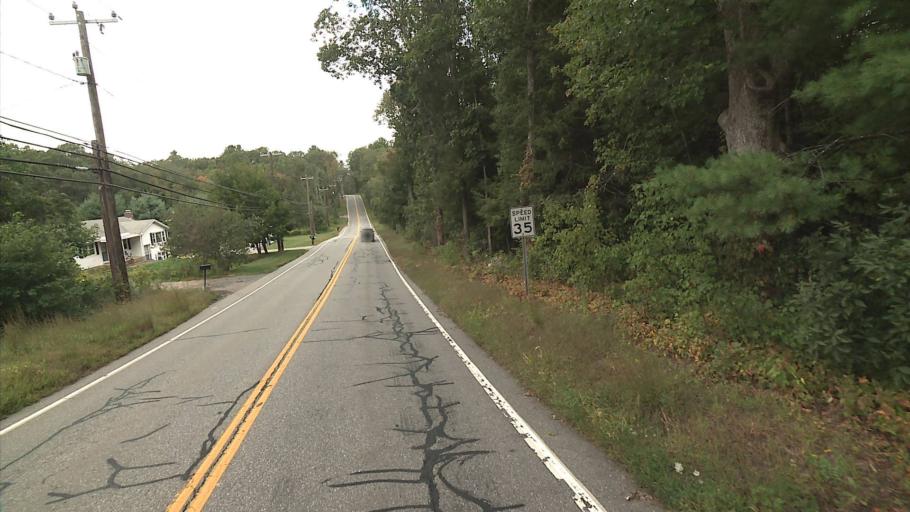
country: US
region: Connecticut
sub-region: Tolland County
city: Storrs
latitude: 41.8362
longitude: -72.2699
